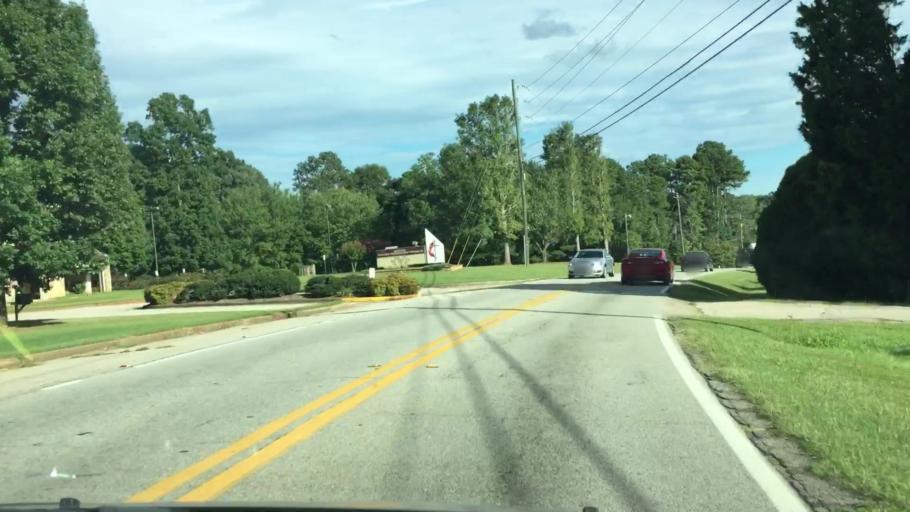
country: US
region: Georgia
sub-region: Henry County
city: Stockbridge
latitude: 33.6150
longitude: -84.2312
